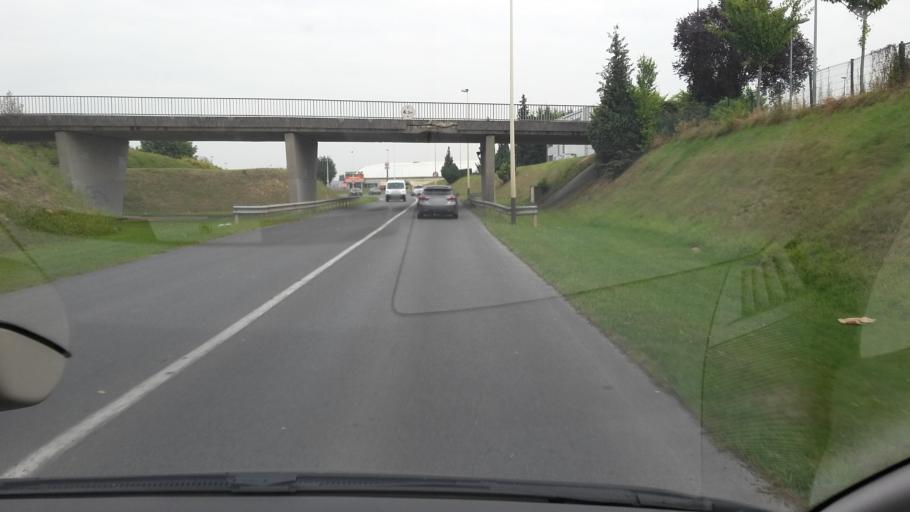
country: FR
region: Champagne-Ardenne
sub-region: Departement de la Marne
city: Cormontreuil
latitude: 49.2177
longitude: 4.0583
